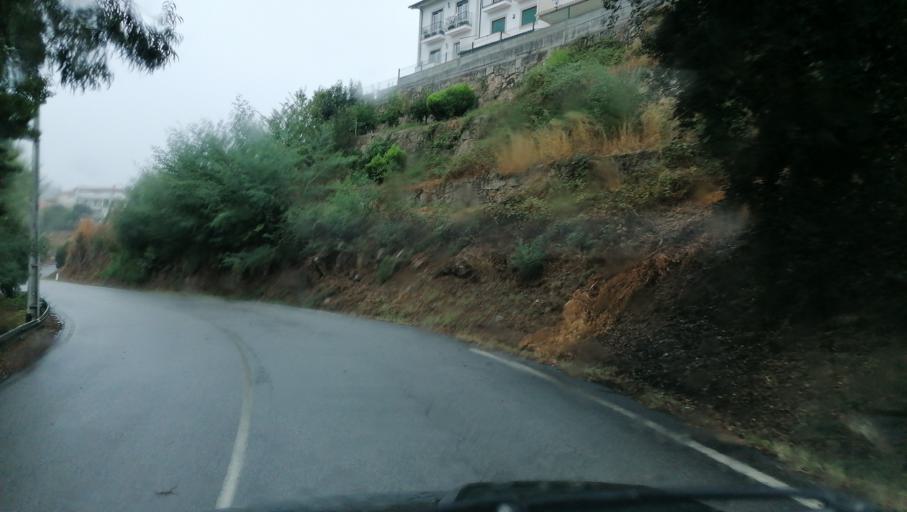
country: PT
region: Braga
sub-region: Cabeceiras de Basto
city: Cabeceiras de Basto
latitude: 41.4890
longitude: -7.9538
